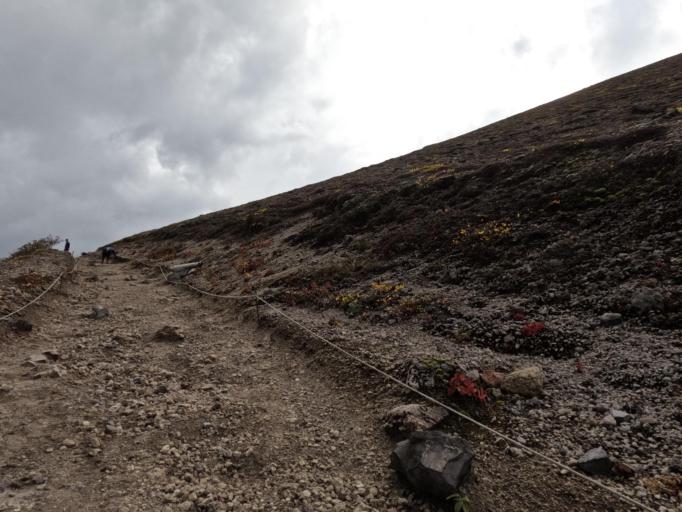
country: JP
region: Hokkaido
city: Shiraoi
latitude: 42.6936
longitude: 141.3903
